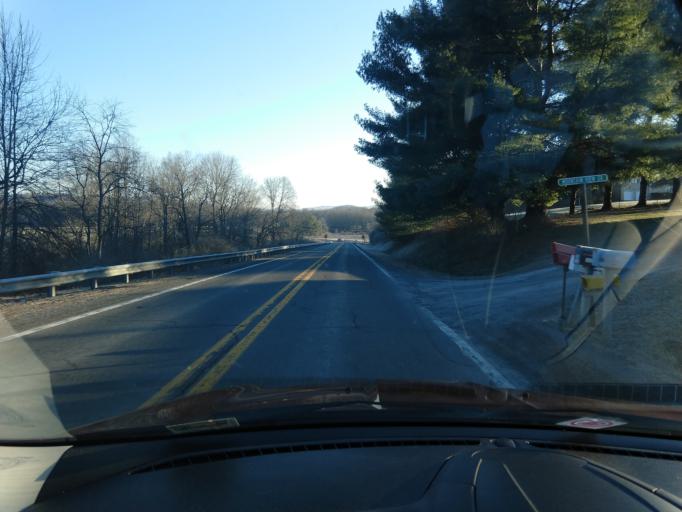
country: US
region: West Virginia
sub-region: Greenbrier County
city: Rainelle
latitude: 37.8548
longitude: -80.7189
